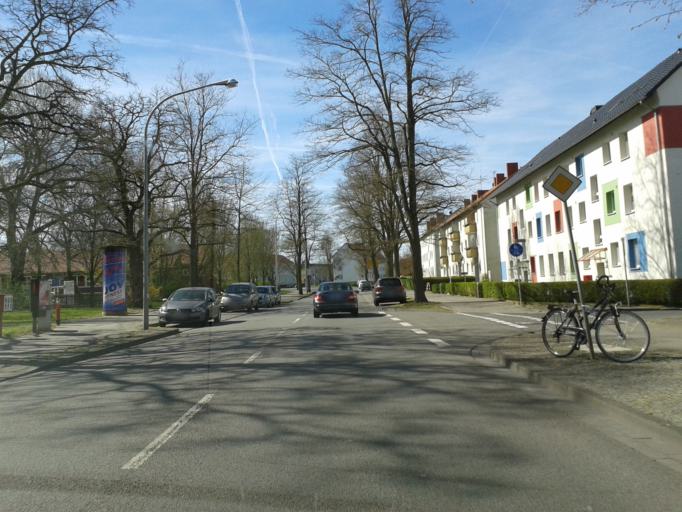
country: DE
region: Lower Saxony
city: Uelzen
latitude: 52.9627
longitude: 10.5750
